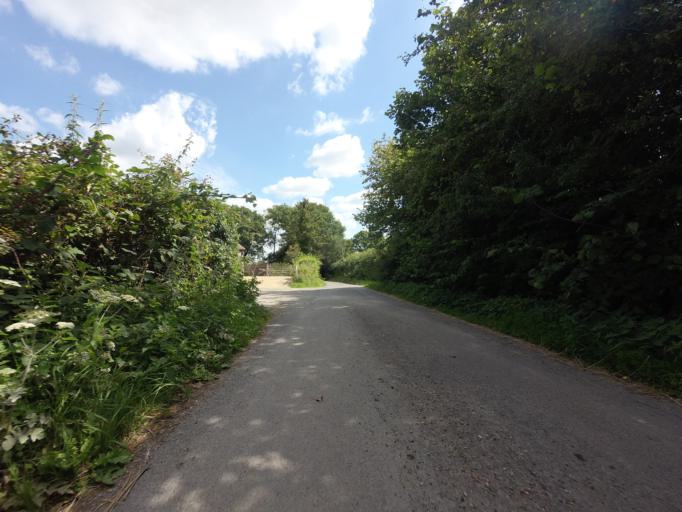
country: GB
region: England
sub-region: Kent
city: Tenterden
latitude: 51.0662
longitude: 0.7140
